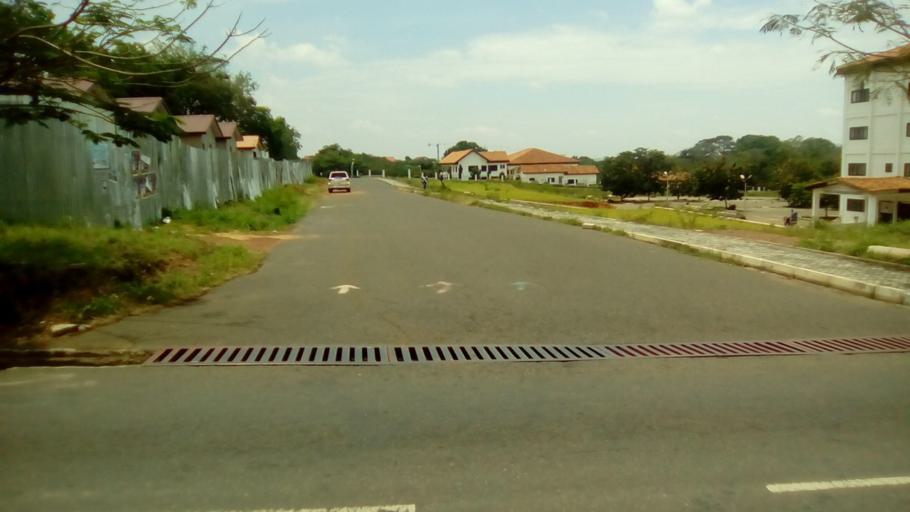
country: GH
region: Greater Accra
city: Medina Estates
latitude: 5.6548
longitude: -0.1824
